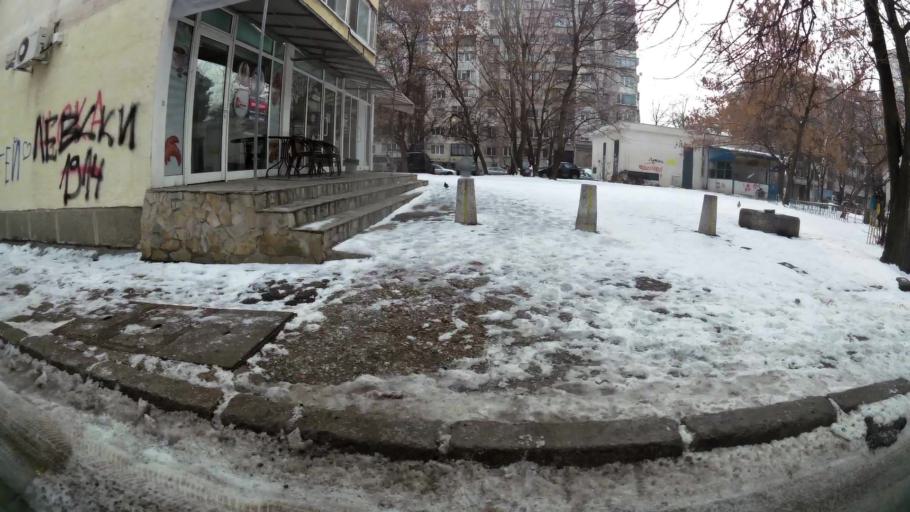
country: BG
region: Sofia-Capital
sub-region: Stolichna Obshtina
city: Sofia
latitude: 42.7106
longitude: 23.2963
